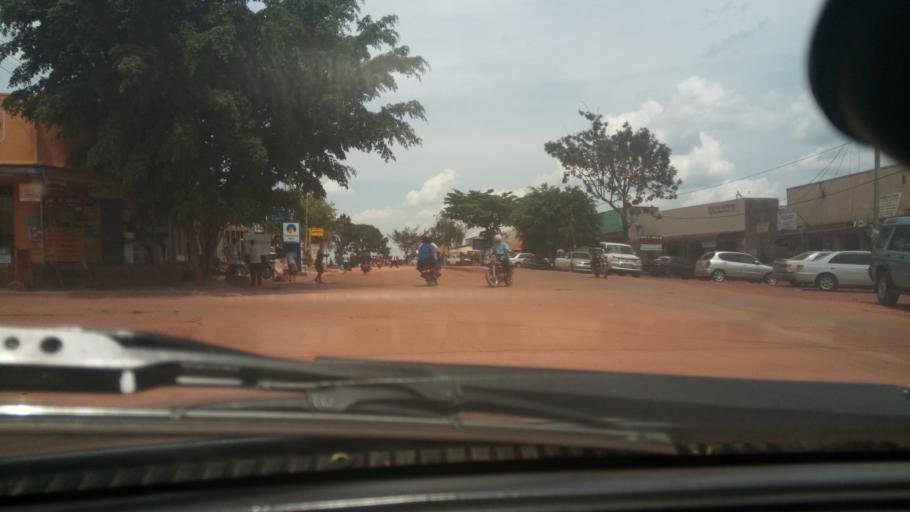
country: UG
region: Central Region
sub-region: Mityana District
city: Mityana
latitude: 0.4006
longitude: 32.0420
